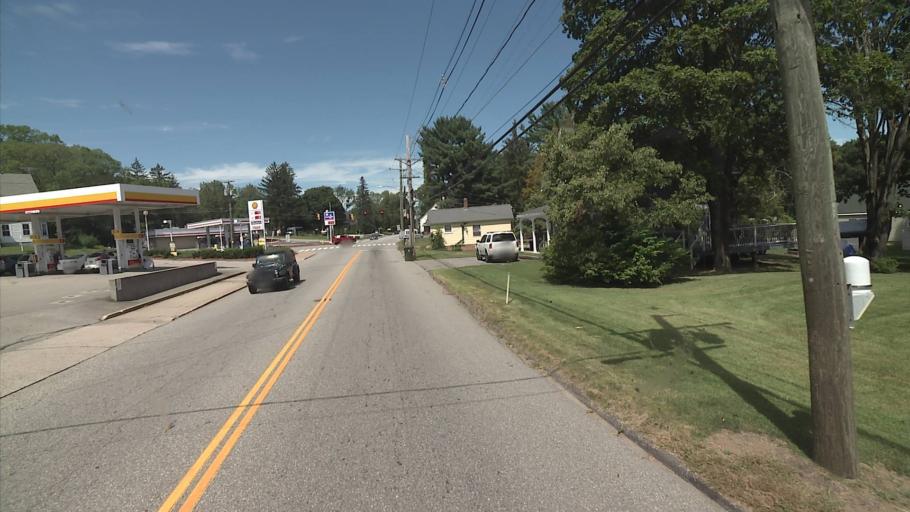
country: US
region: Connecticut
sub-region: Windham County
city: Willimantic
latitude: 41.7207
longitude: -72.2023
